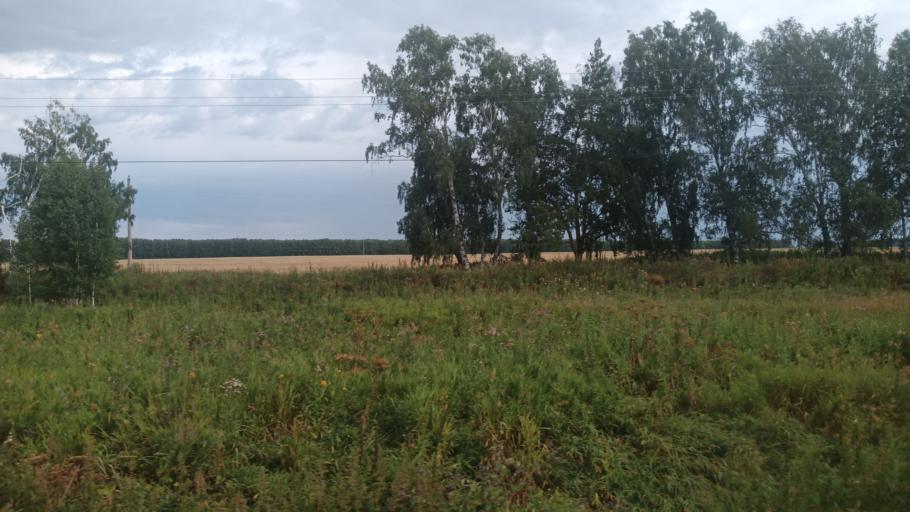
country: RU
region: Altai Krai
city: Nalobikha
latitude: 53.2362
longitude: 84.4695
